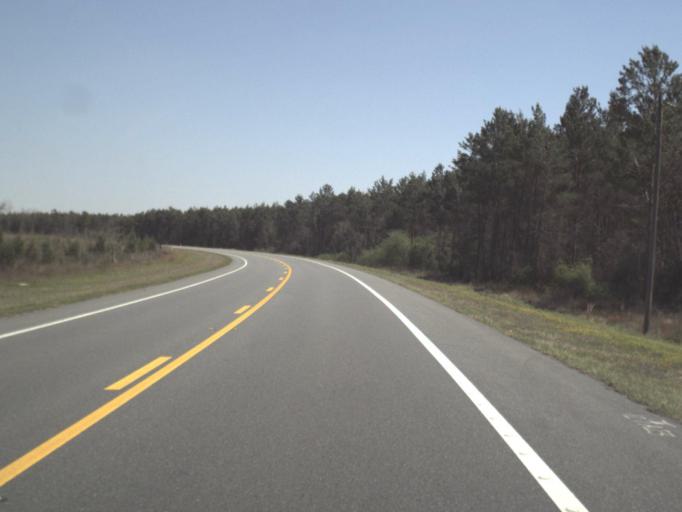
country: US
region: Florida
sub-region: Bay County
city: Youngstown
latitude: 30.4222
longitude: -85.3111
